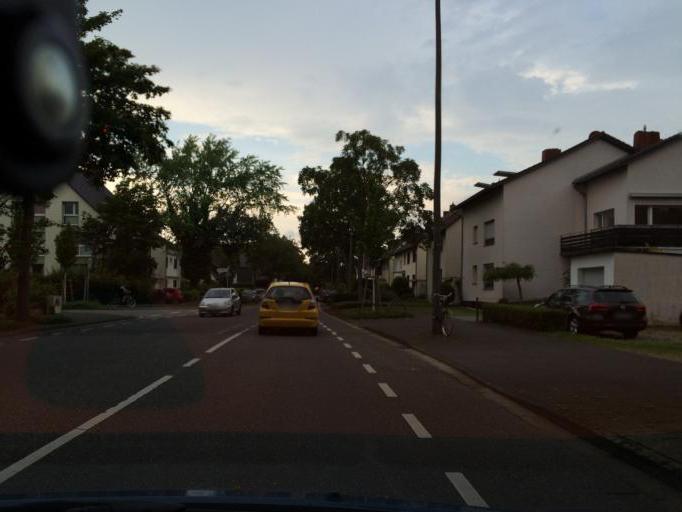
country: DE
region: North Rhine-Westphalia
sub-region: Regierungsbezirk Koln
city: Bonn
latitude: 50.7330
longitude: 7.1228
